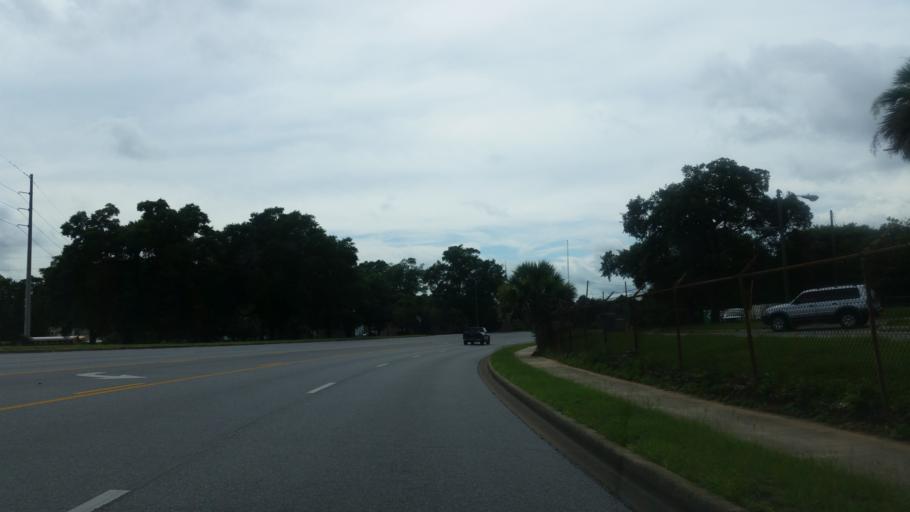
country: US
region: Florida
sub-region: Escambia County
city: Goulding
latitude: 30.4386
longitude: -87.2242
